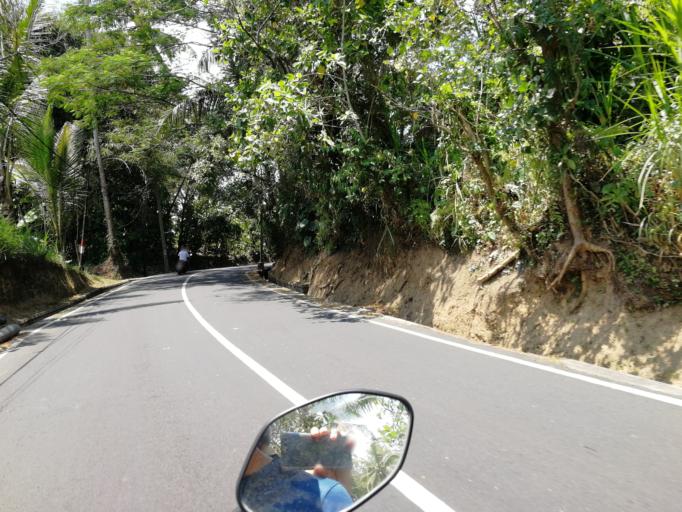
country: ID
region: Bali
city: Banjar Kubu
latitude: -8.4492
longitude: 115.3871
